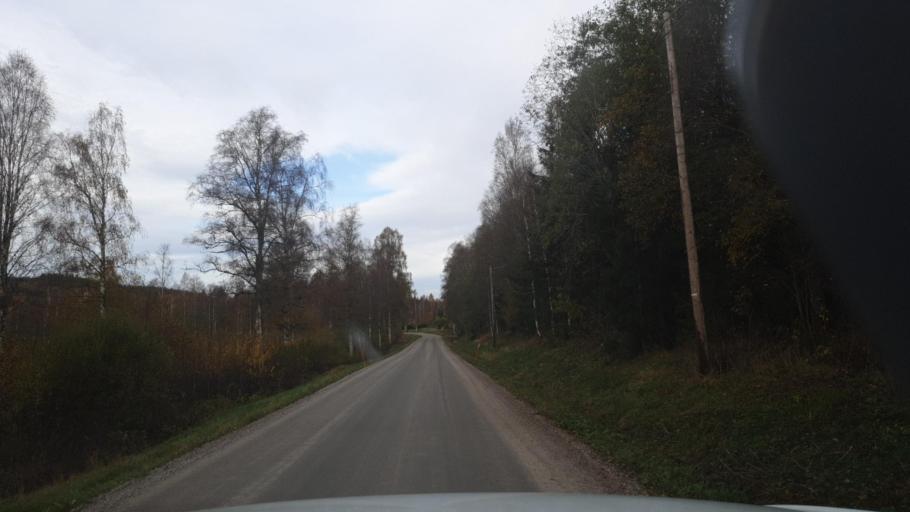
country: SE
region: Vaermland
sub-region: Arvika Kommun
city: Arvika
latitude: 59.7464
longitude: 12.8301
